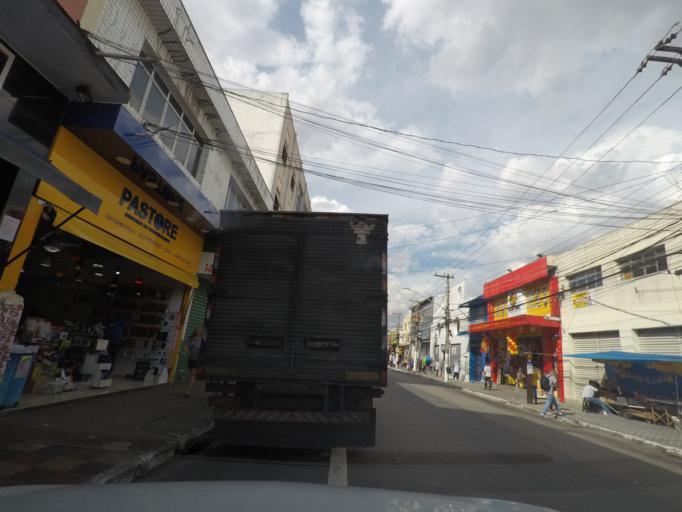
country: BR
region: Sao Paulo
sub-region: Diadema
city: Diadema
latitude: -23.6535
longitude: -46.7038
